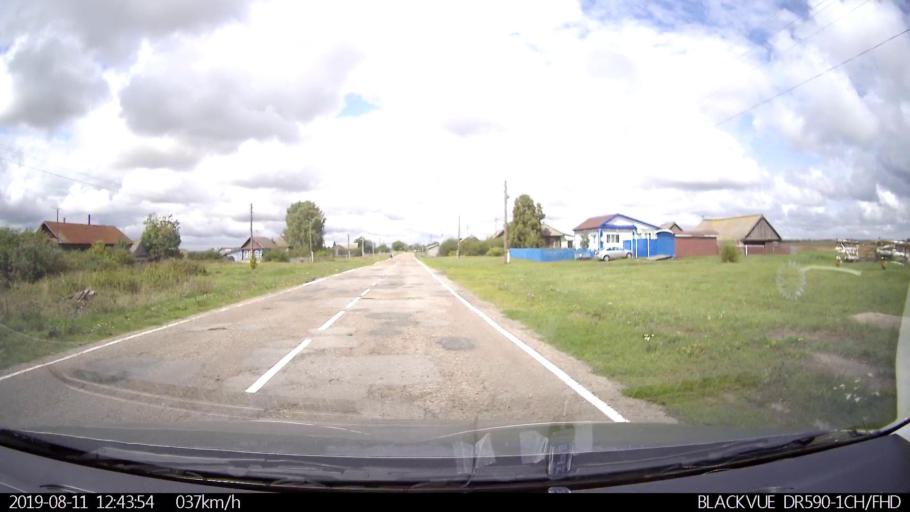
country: RU
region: Ulyanovsk
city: Ignatovka
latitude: 53.8525
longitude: 47.7401
